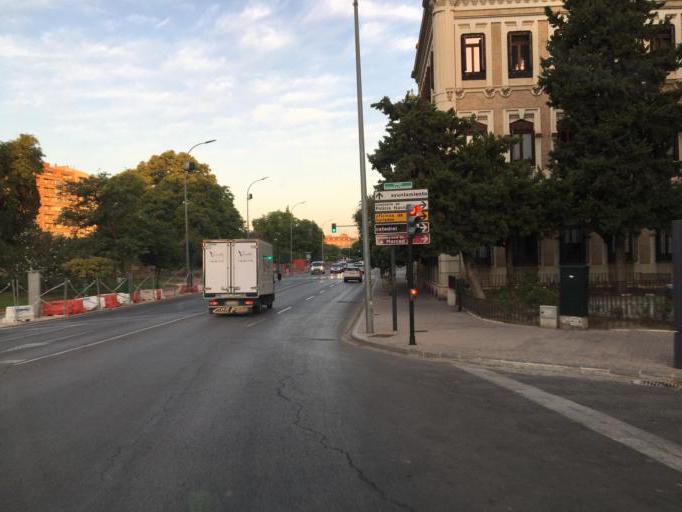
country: ES
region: Murcia
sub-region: Murcia
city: Murcia
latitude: 37.9822
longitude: -1.1267
